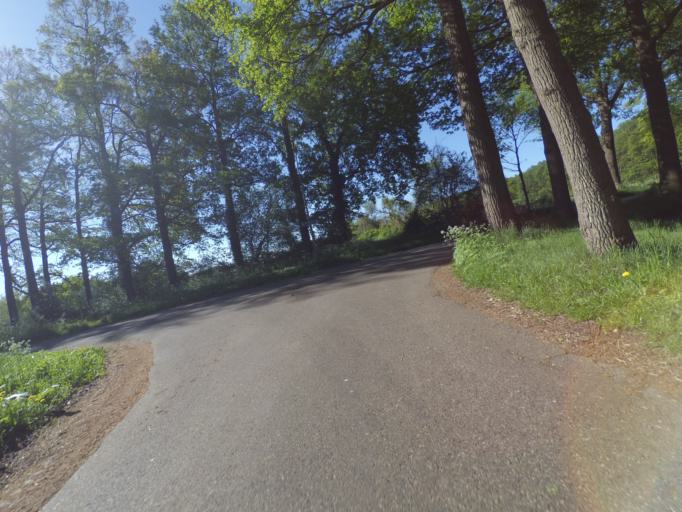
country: NL
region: Gelderland
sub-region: Gemeente Brummen
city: Brummen
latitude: 52.1232
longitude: 6.1165
